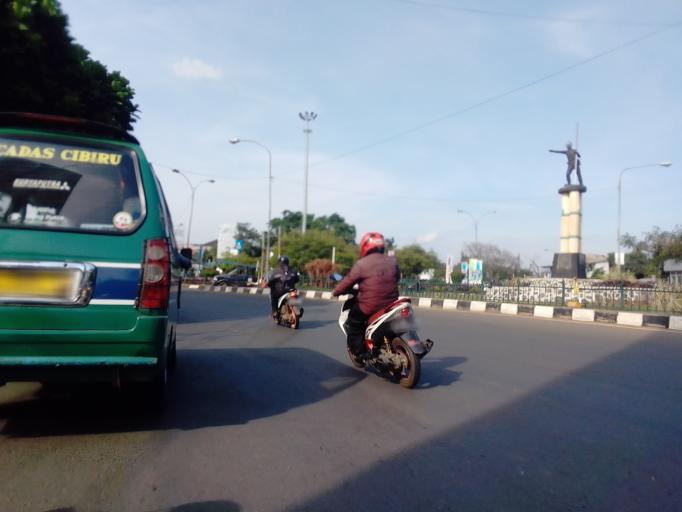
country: ID
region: West Java
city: Cileunyi
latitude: -6.9351
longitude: 107.7171
